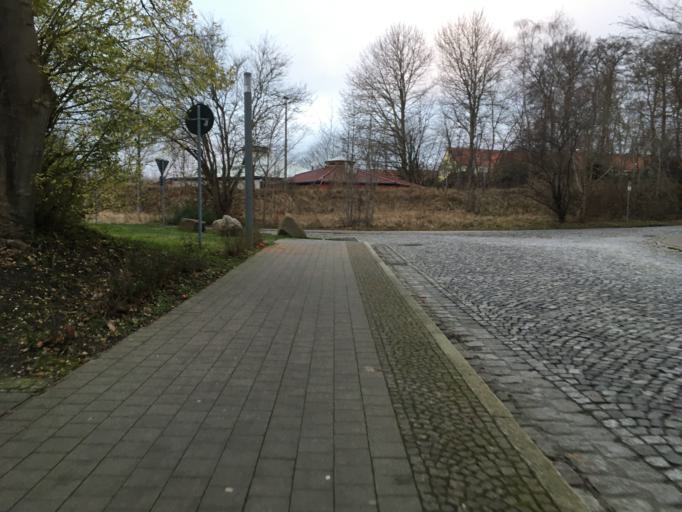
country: DE
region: Mecklenburg-Vorpommern
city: Sassnitz
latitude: 54.5085
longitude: 13.6260
